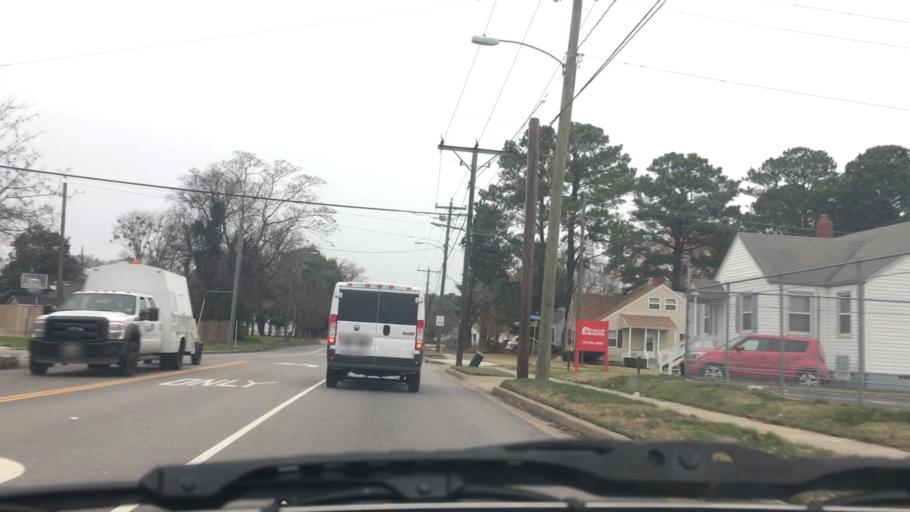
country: US
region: Virginia
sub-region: City of Norfolk
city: Norfolk
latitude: 36.8811
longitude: -76.2553
